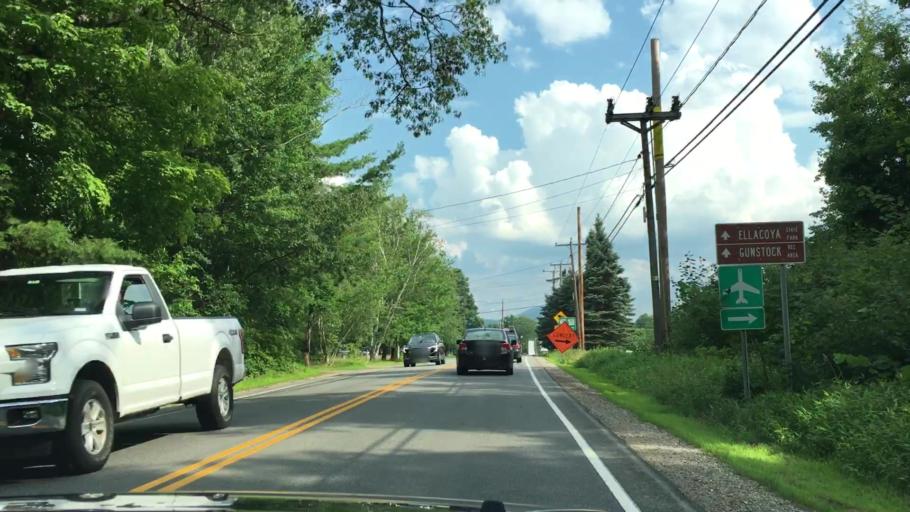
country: US
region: New Hampshire
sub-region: Belknap County
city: Gilford
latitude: 43.5897
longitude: -71.4222
